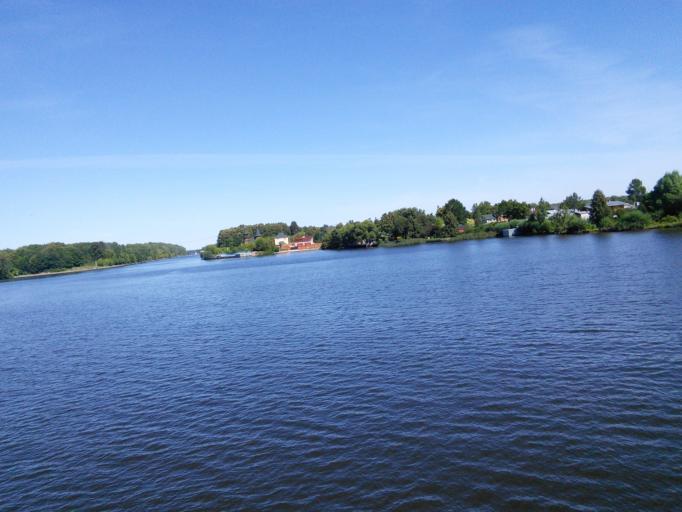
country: RU
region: Moskovskaya
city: Pirogovskiy
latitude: 56.0419
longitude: 37.6681
